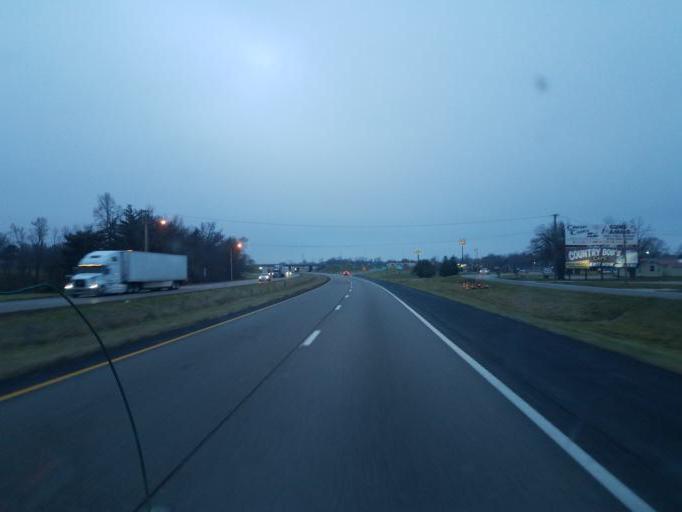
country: US
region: Missouri
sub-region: Phelps County
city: Saint James
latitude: 38.0075
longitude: -91.6144
